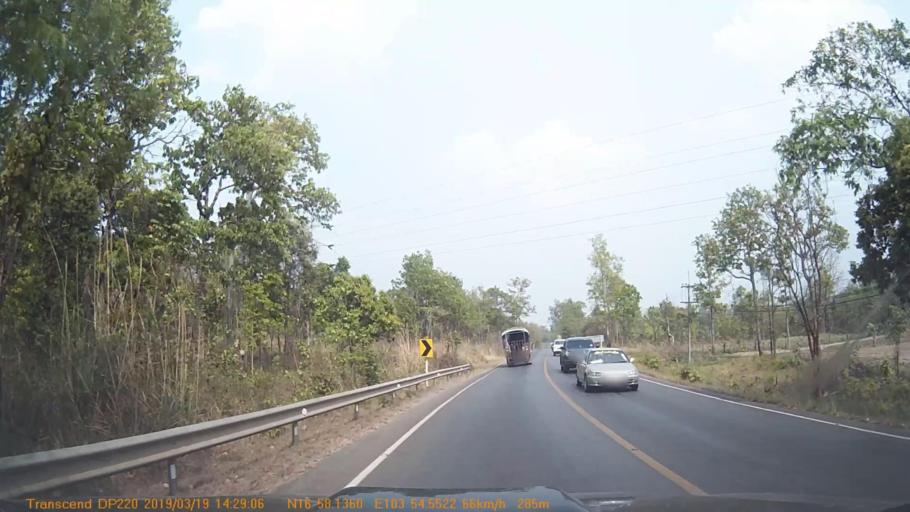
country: TH
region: Sakon Nakhon
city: Phu Phan
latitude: 16.9691
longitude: 103.9097
